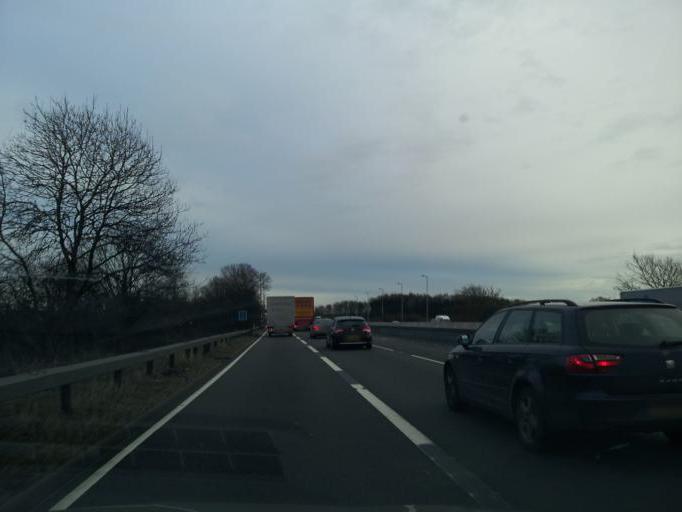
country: GB
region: England
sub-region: Northamptonshire
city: Long Buckby
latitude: 52.2525
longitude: -1.0732
